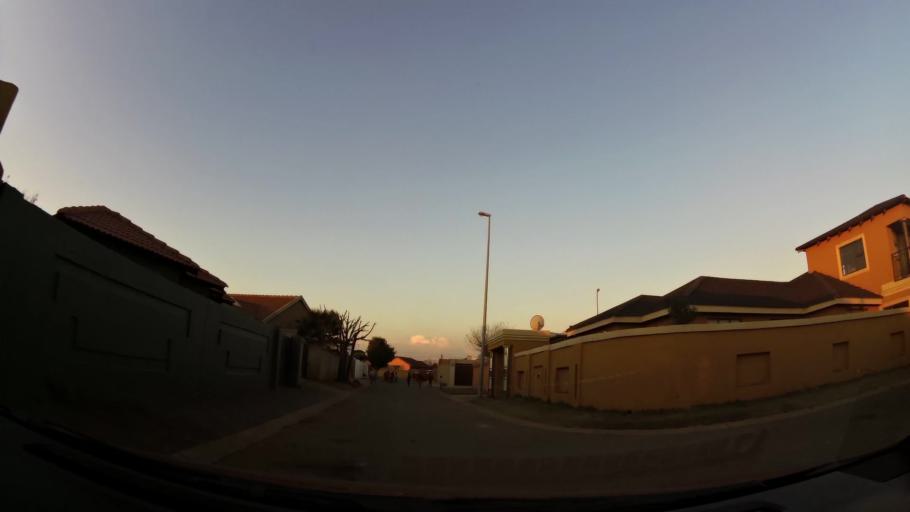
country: ZA
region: Gauteng
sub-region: City of Johannesburg Metropolitan Municipality
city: Soweto
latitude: -26.2286
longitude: 27.8422
